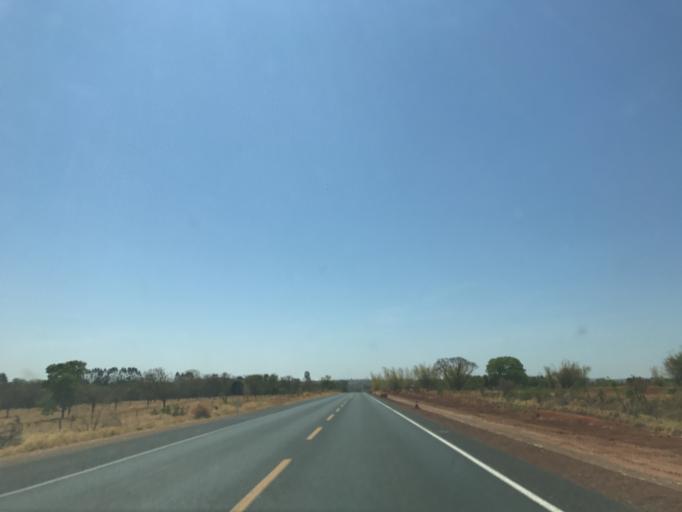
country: BR
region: Minas Gerais
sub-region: Prata
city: Prata
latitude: -19.3776
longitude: -48.8984
